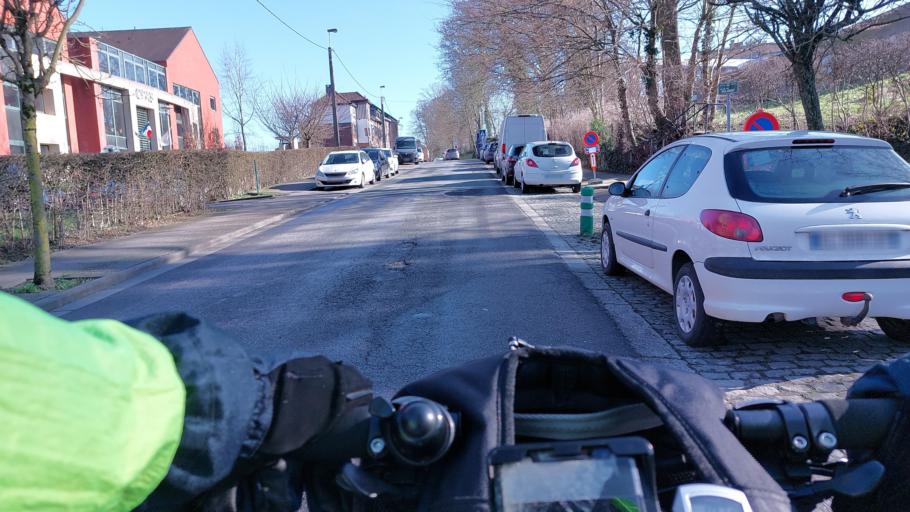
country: BE
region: Wallonia
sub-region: Province du Brabant Wallon
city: Nivelles
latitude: 50.5955
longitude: 4.3150
